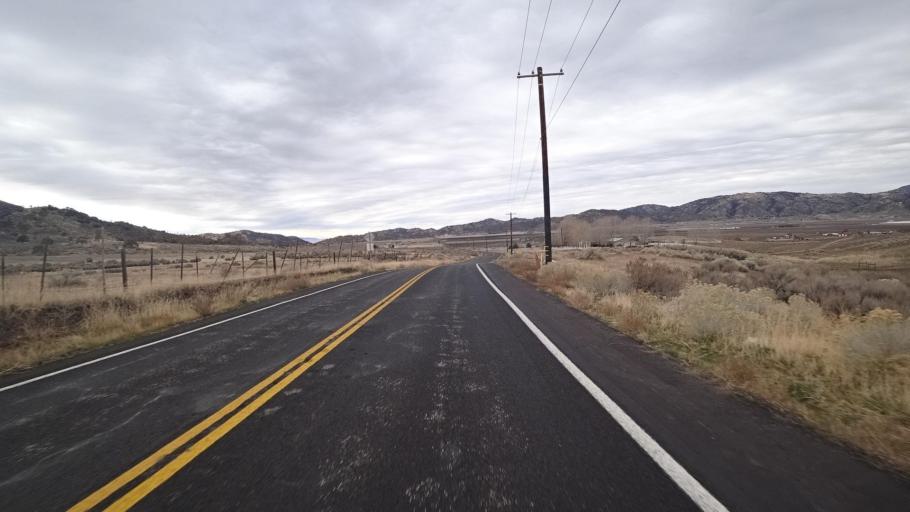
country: US
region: California
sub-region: Kern County
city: Stallion Springs
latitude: 35.0942
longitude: -118.5873
